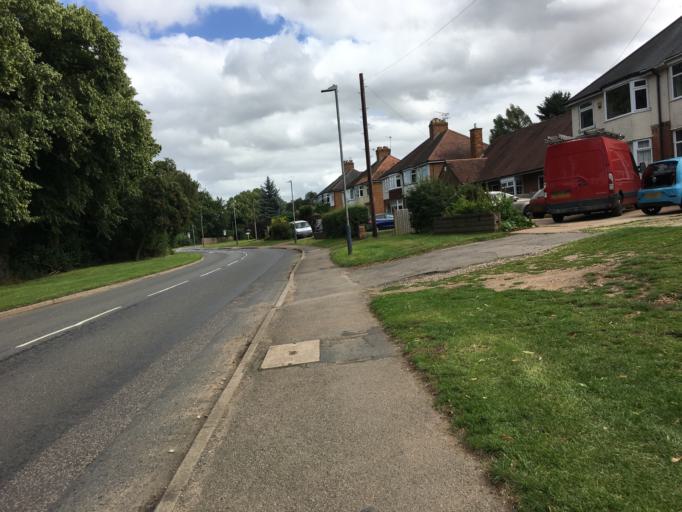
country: GB
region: England
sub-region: Warwickshire
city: Rugby
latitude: 52.3811
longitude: -1.2294
